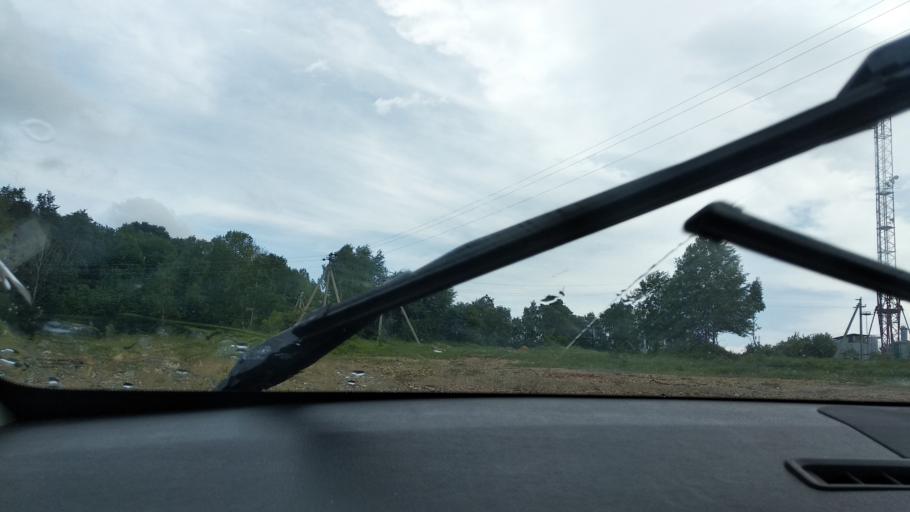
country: RU
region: Adygeya
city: Kamennomostskiy
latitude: 44.2230
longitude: 39.9948
